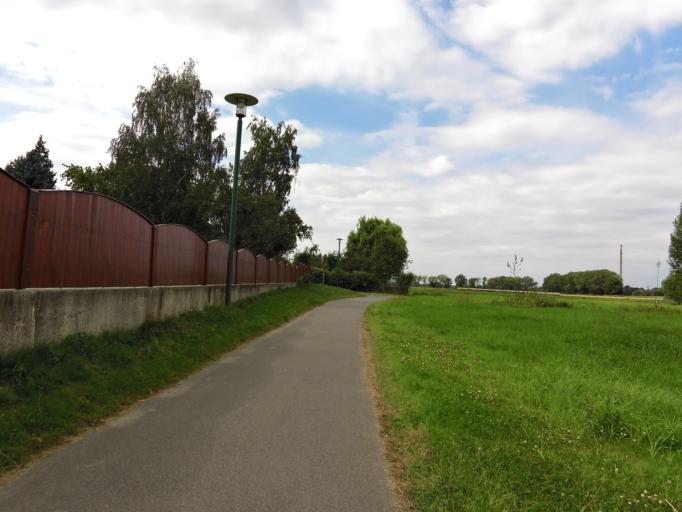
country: DE
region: Saxony
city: Coswig
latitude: 51.0985
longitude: 13.5940
